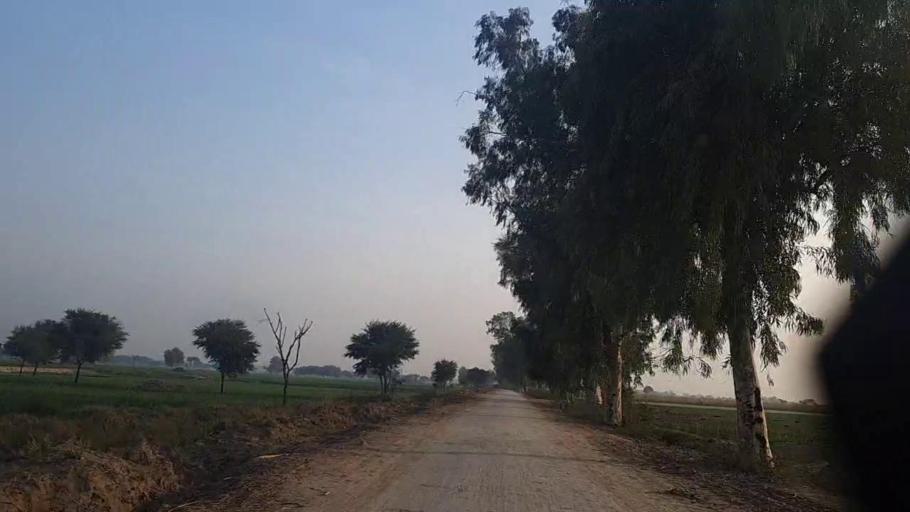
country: PK
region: Sindh
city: Sakrand
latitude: 26.1289
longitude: 68.2292
